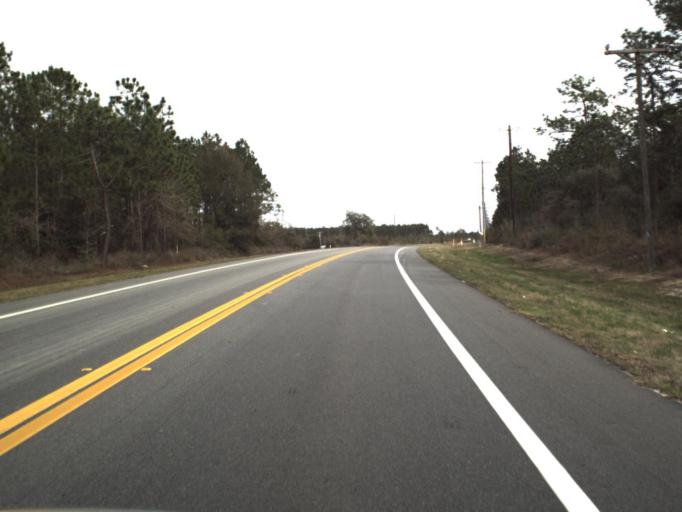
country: US
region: Florida
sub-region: Bay County
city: Callaway
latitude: 30.1525
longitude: -85.4917
